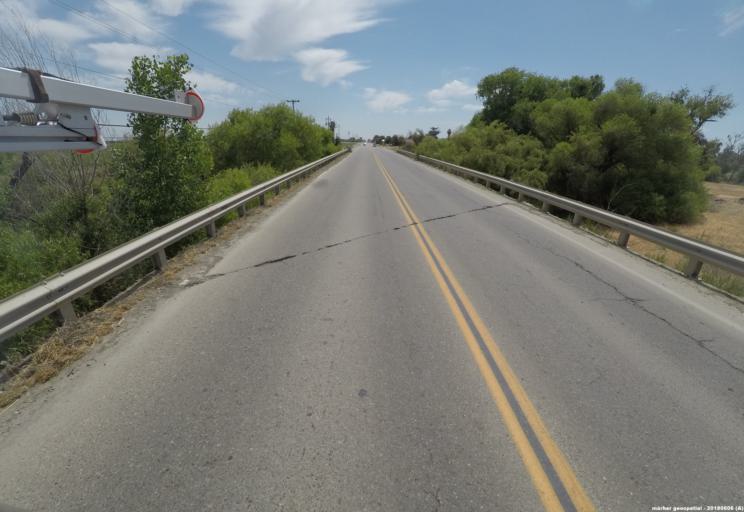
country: US
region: California
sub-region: Fresno County
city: Firebaugh
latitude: 36.8583
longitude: -120.4452
